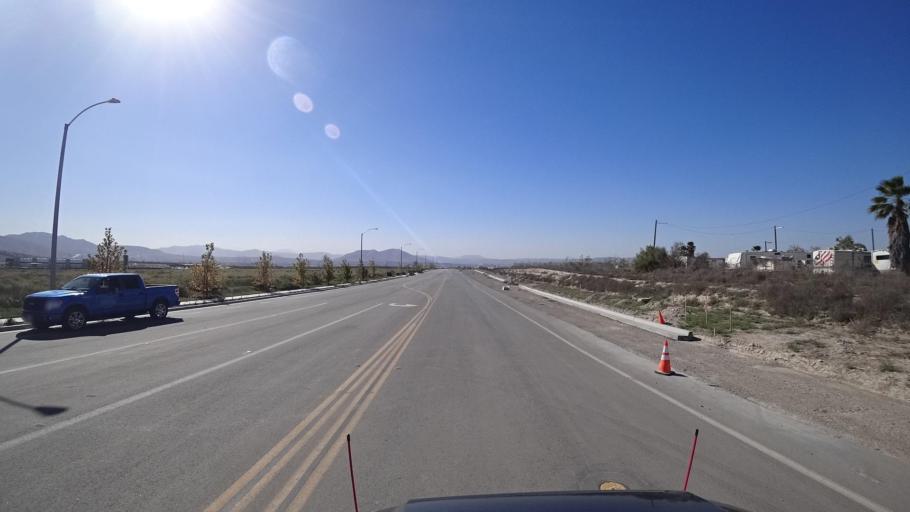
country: MX
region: Baja California
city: Tijuana
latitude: 32.5669
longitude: -116.9192
